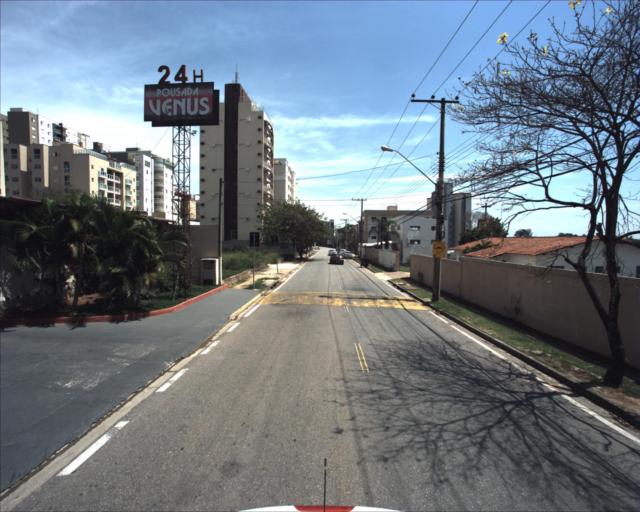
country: BR
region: Sao Paulo
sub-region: Sorocaba
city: Sorocaba
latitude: -23.5321
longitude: -47.4694
